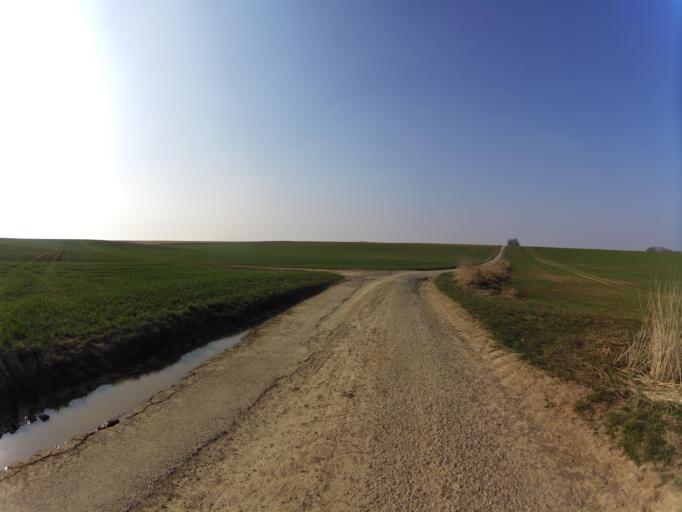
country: DE
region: Bavaria
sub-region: Regierungsbezirk Unterfranken
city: Winterhausen
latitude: 49.6859
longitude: 9.9857
